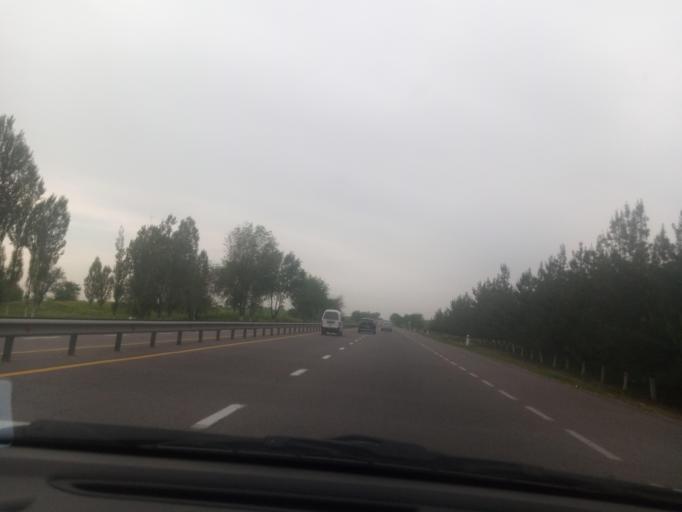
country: UZ
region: Toshkent
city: Tuytepa
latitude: 41.1165
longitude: 69.4446
